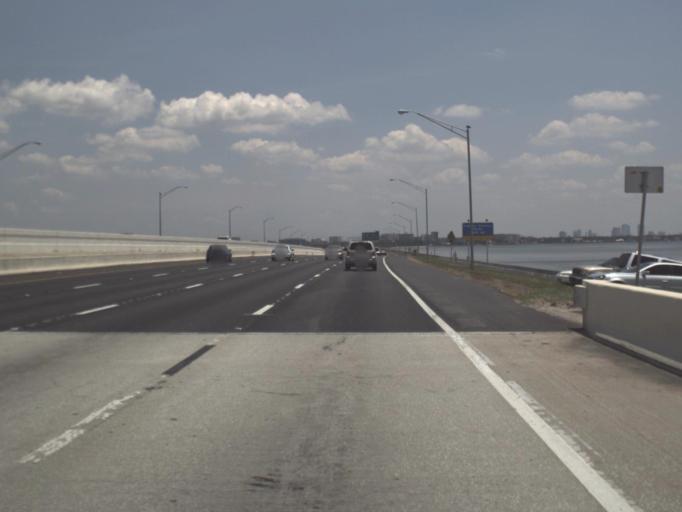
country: US
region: Florida
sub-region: Hillsborough County
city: Town 'n' Country
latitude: 27.9360
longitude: -82.5641
